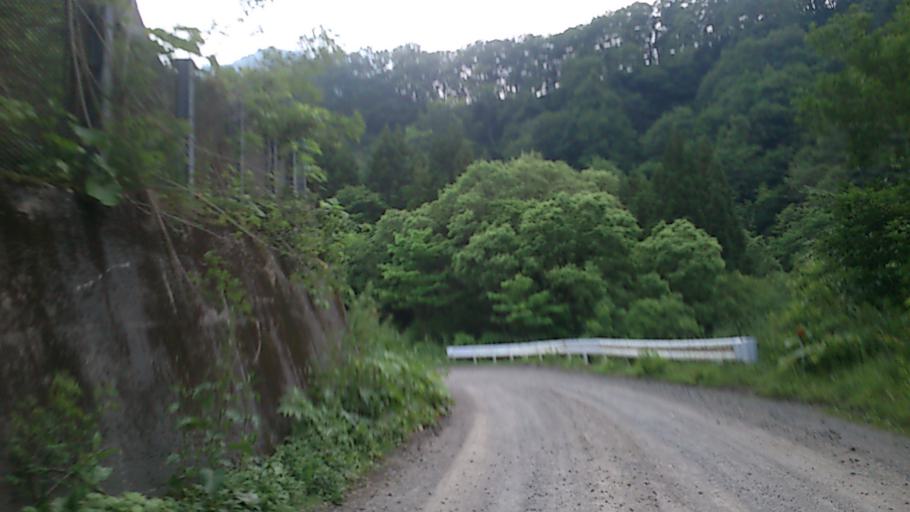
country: JP
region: Aomori
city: Hirosaki
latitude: 40.5251
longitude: 140.1782
